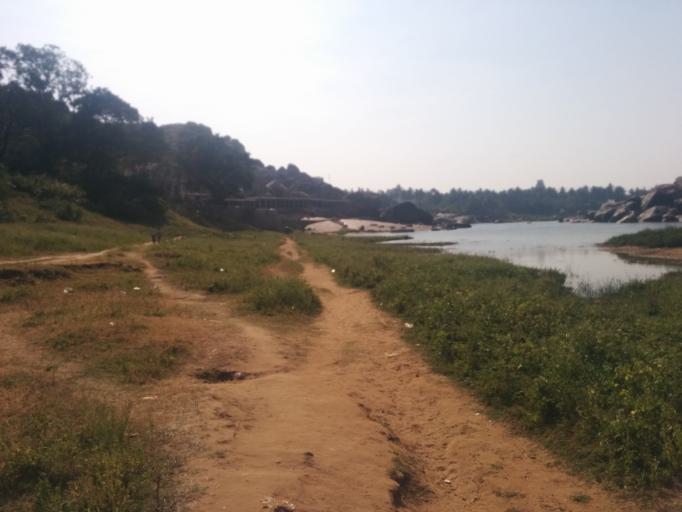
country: IN
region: Karnataka
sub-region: Bellary
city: Hampi
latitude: 15.3369
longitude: 76.4694
